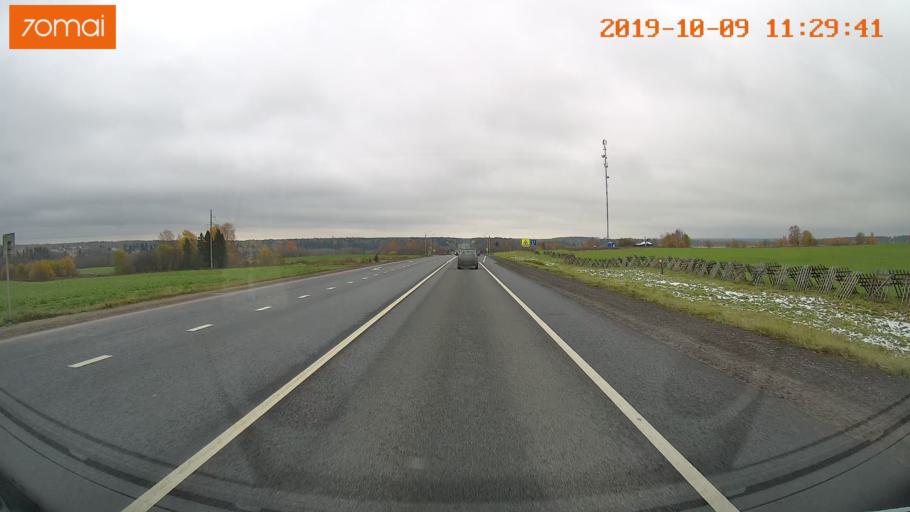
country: RU
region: Vologda
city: Vologda
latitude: 59.0601
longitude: 40.0590
